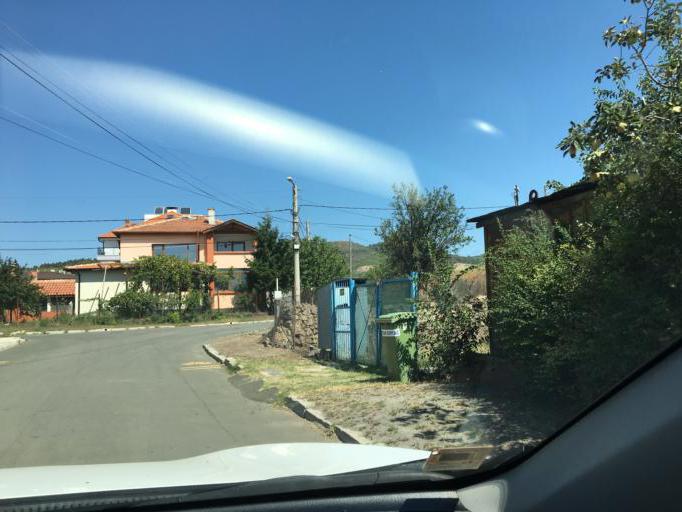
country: BG
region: Burgas
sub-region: Obshtina Kameno
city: Kameno
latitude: 42.6299
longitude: 27.3916
